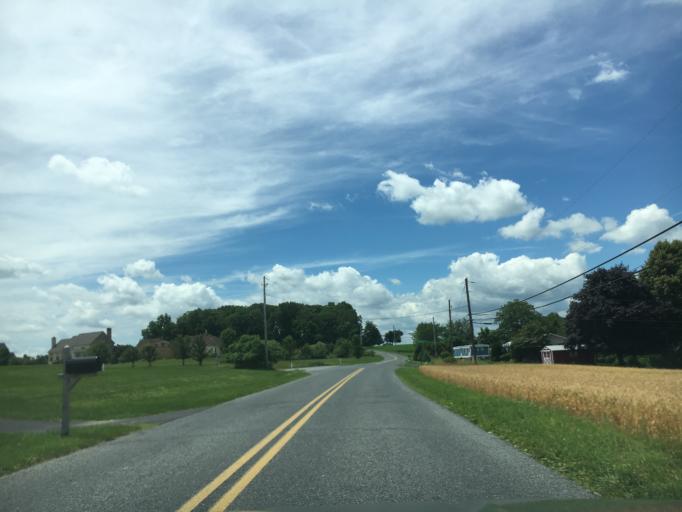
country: US
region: Pennsylvania
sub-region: Lehigh County
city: Laurys Station
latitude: 40.7107
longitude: -75.5606
